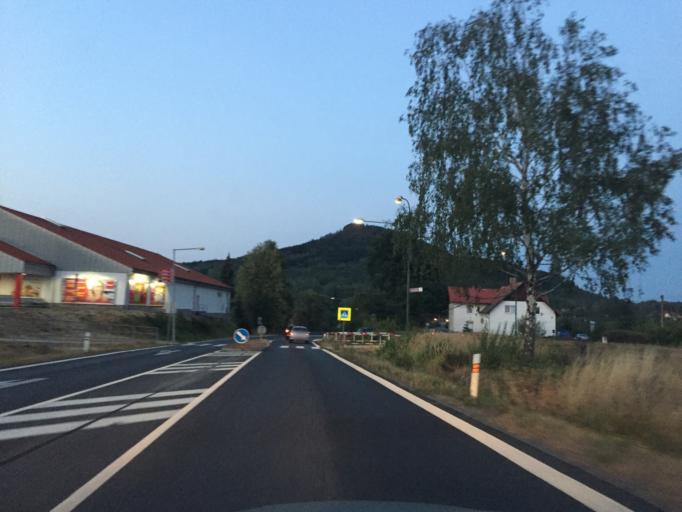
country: CZ
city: Cvikov
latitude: 50.7749
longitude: 14.6352
